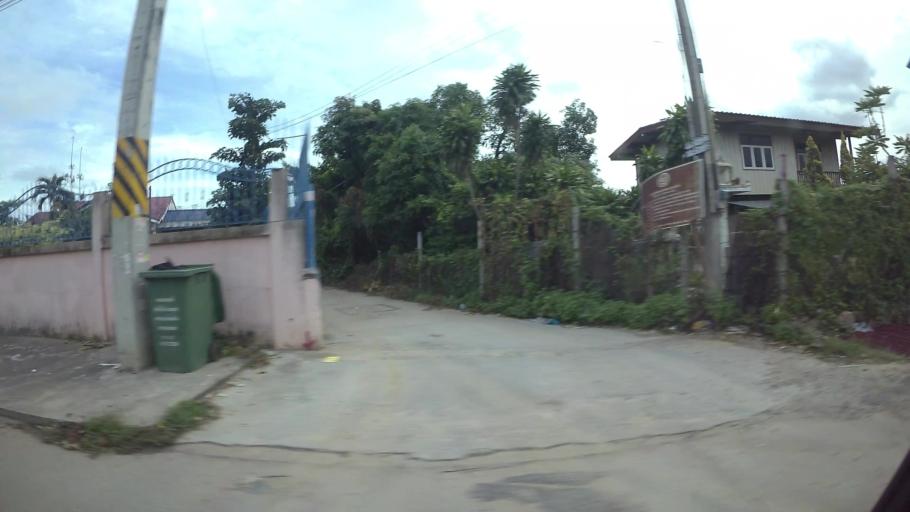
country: TH
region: Chon Buri
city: Si Racha
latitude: 13.1294
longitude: 100.9697
